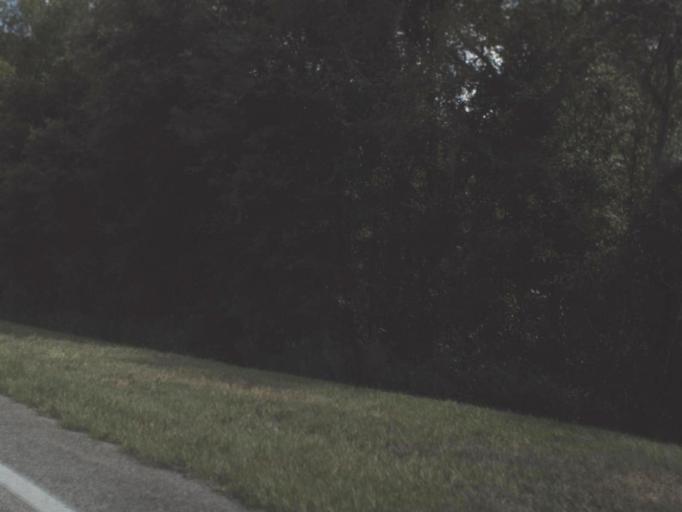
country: US
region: Florida
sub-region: Pasco County
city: Zephyrhills North
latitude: 28.2918
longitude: -82.0555
